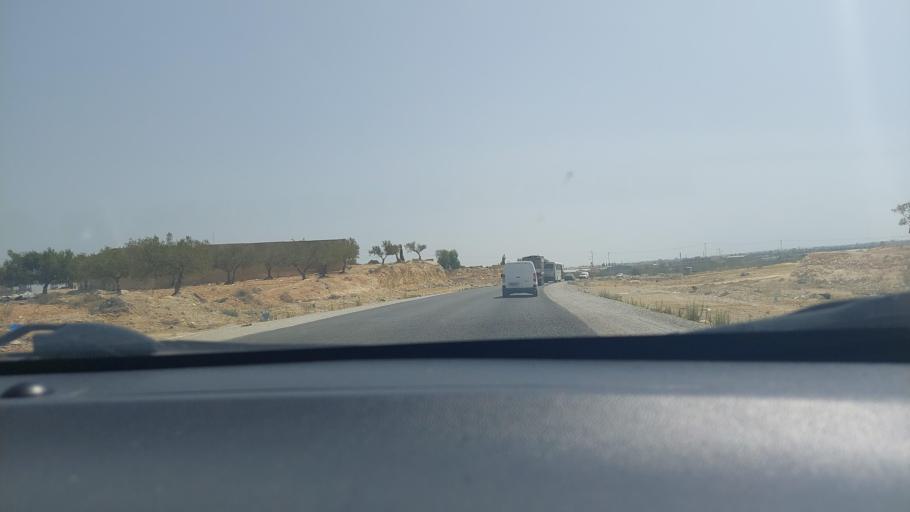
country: TN
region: Al Munastir
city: Qasr Hallal
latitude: 35.6370
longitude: 10.8689
